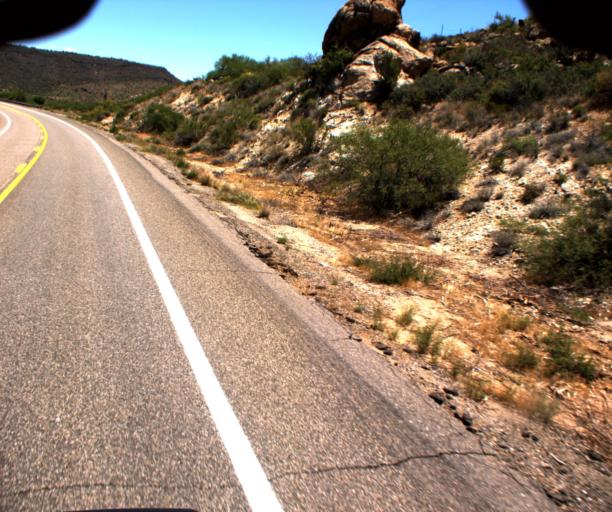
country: US
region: Arizona
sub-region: Yavapai County
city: Bagdad
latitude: 34.5167
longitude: -113.0889
